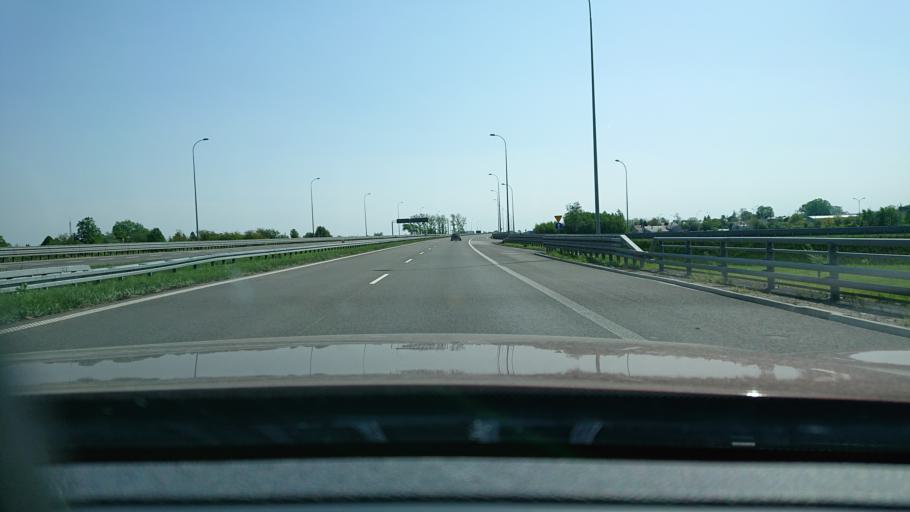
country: PL
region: Subcarpathian Voivodeship
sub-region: Powiat lancucki
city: Lancut
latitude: 50.0992
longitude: 22.2242
